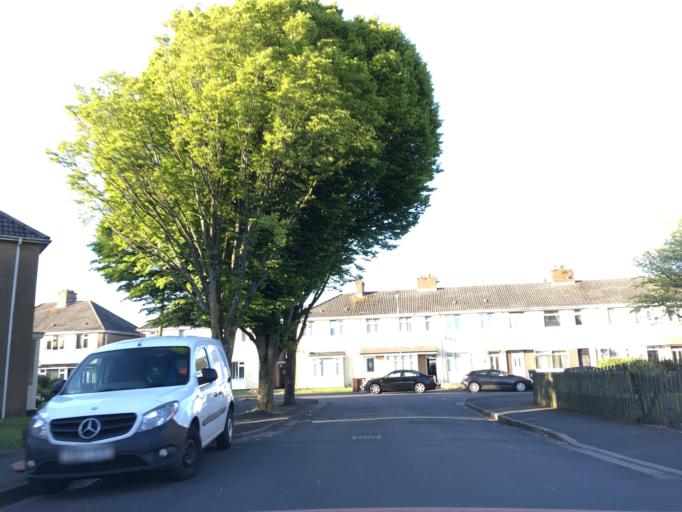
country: GB
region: Wales
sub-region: Newport
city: Newport
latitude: 51.5691
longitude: -3.0139
